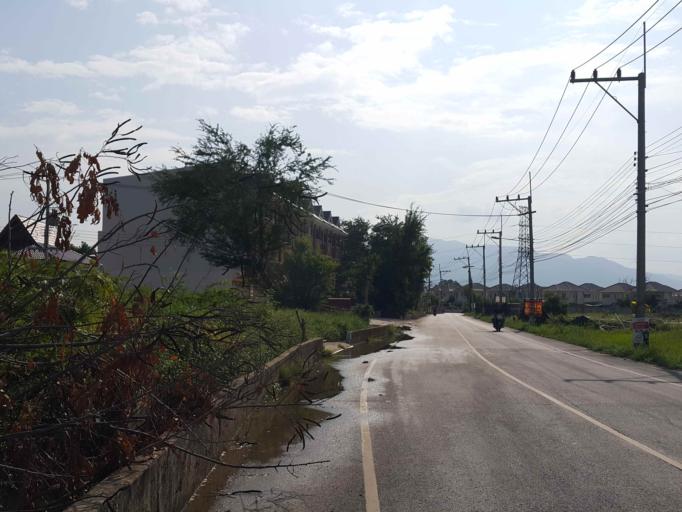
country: TH
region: Chiang Mai
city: San Sai
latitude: 18.8305
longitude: 99.0286
